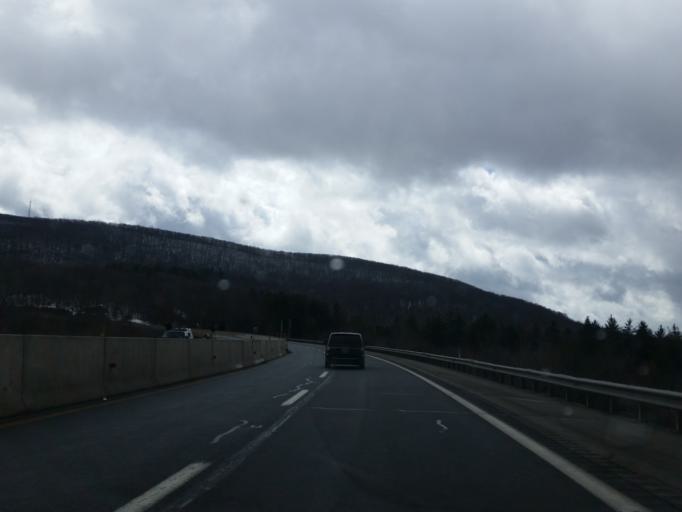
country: US
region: Pennsylvania
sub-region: Lackawanna County
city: Clarks Summit
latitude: 41.4738
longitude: -75.7037
